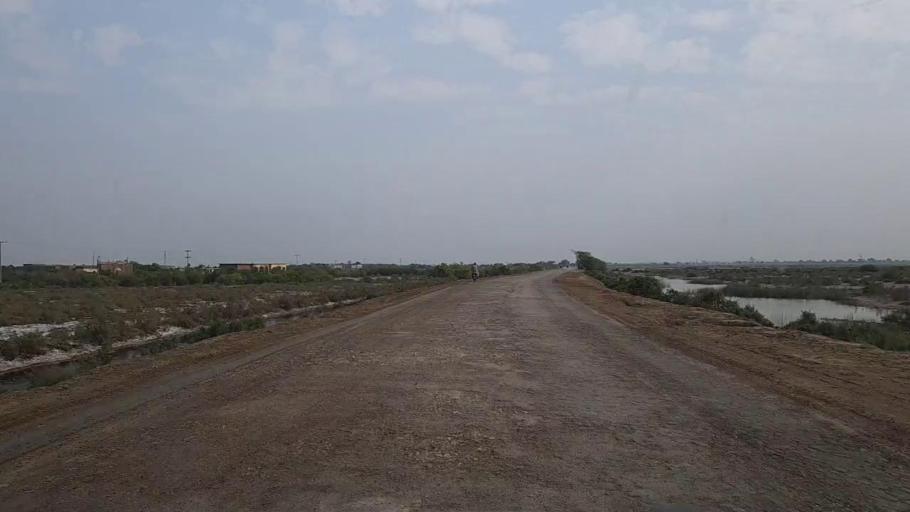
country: PK
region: Sindh
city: Mirwah Gorchani
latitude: 25.3793
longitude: 69.0944
